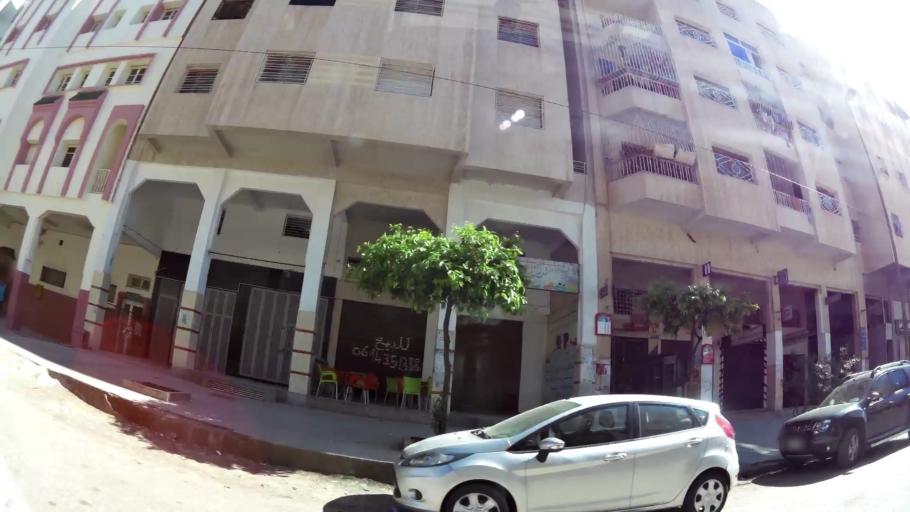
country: MA
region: Fes-Boulemane
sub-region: Fes
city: Fes
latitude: 34.0146
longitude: -4.9724
